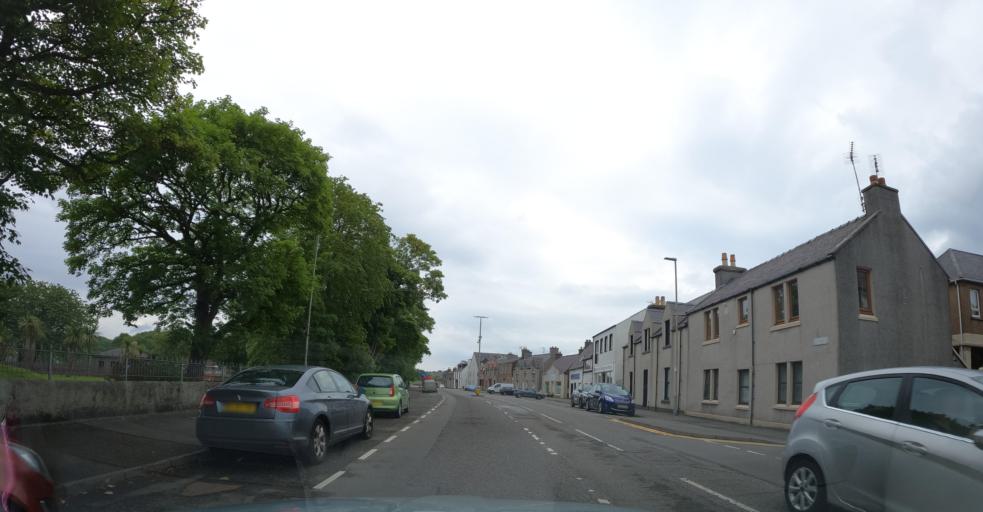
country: GB
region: Scotland
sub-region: Eilean Siar
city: Stornoway
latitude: 58.2138
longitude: -6.3863
